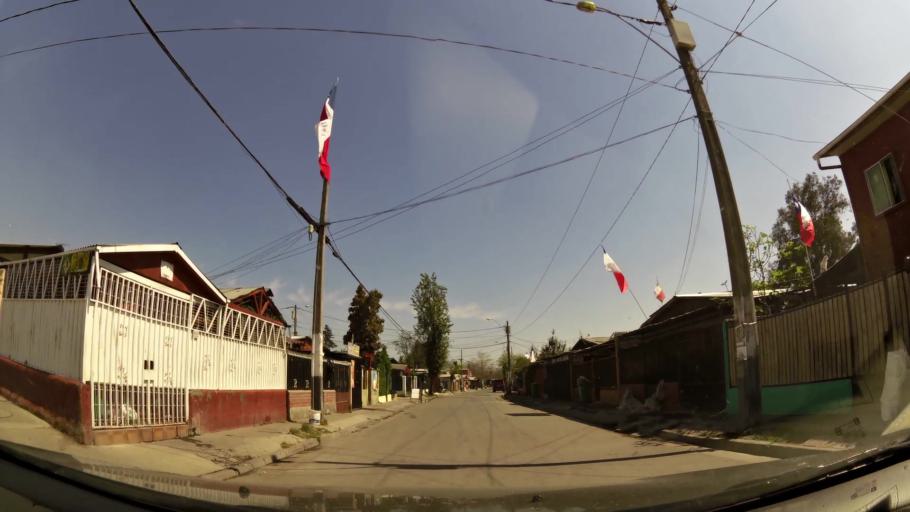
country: CL
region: Santiago Metropolitan
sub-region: Provincia de Santiago
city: La Pintana
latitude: -33.5888
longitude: -70.6263
